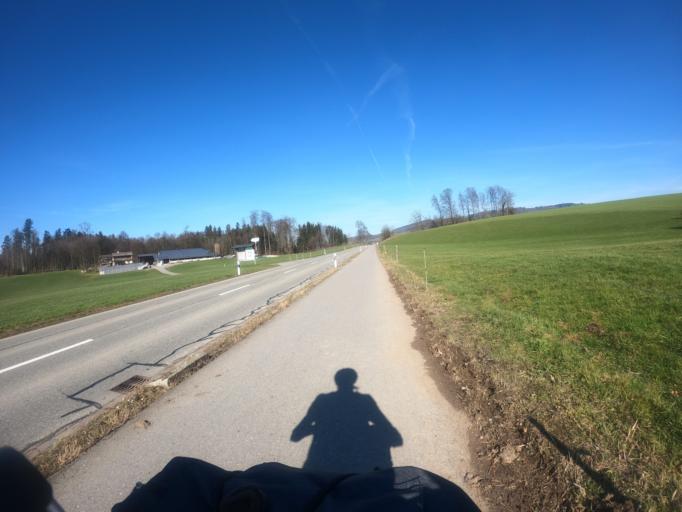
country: CH
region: Zurich
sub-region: Bezirk Affoltern
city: Mettmenstetten
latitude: 47.2373
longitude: 8.4507
